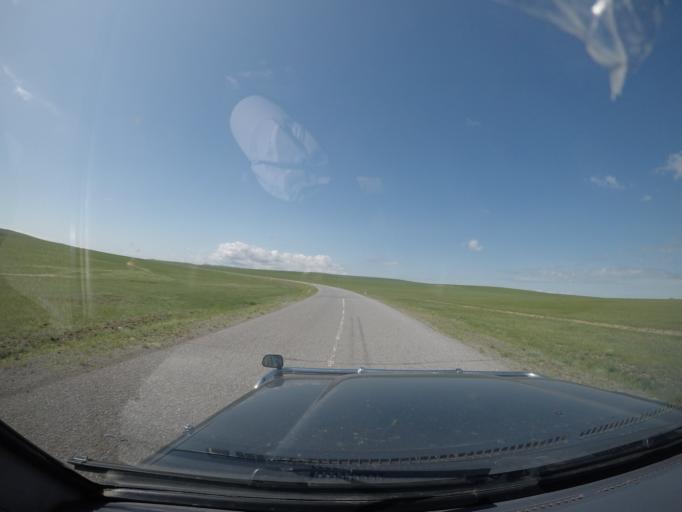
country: MN
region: Hentiy
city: Bayan
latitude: 47.3157
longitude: 111.3396
